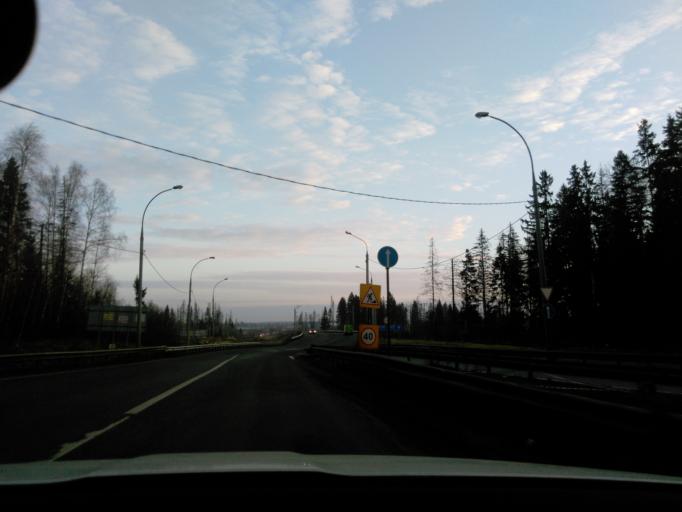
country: RU
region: Moskovskaya
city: Novopodrezkovo
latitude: 55.9693
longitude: 37.3283
